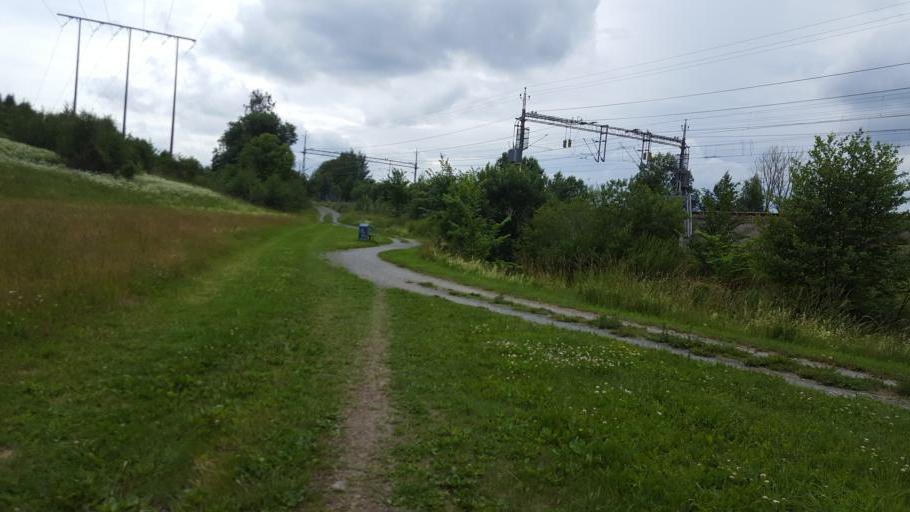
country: SE
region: Stockholm
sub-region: Upplands Vasby Kommun
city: Upplands Vaesby
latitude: 59.5053
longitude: 17.8925
